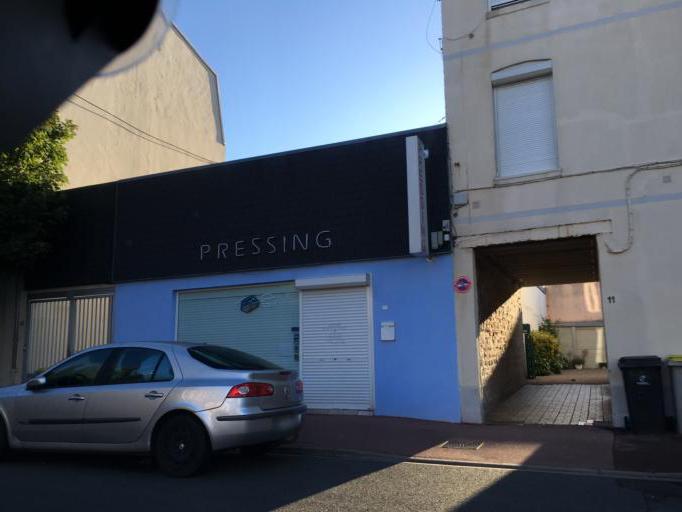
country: FR
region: Nord-Pas-de-Calais
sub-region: Departement du Pas-de-Calais
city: Berck-Plage
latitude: 50.4038
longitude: 1.5655
